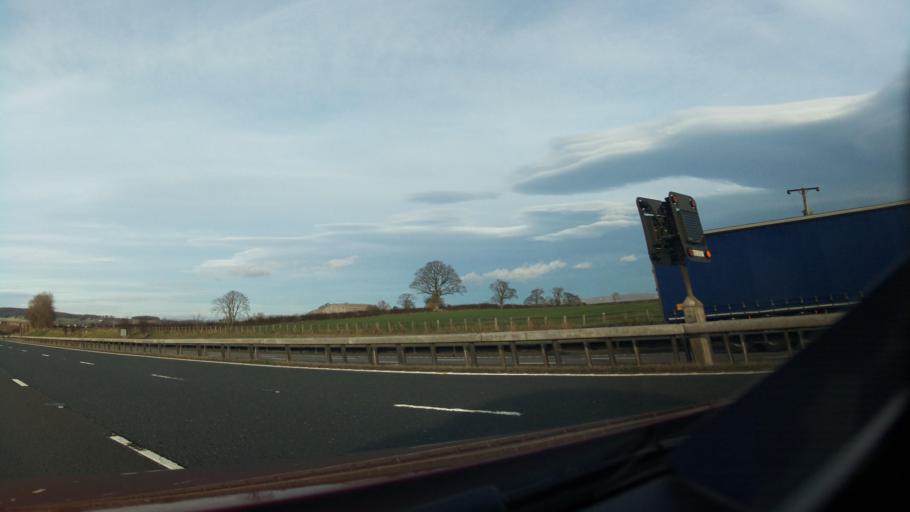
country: GB
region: England
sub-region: Cumbria
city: Penrith
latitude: 54.6201
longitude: -2.7207
